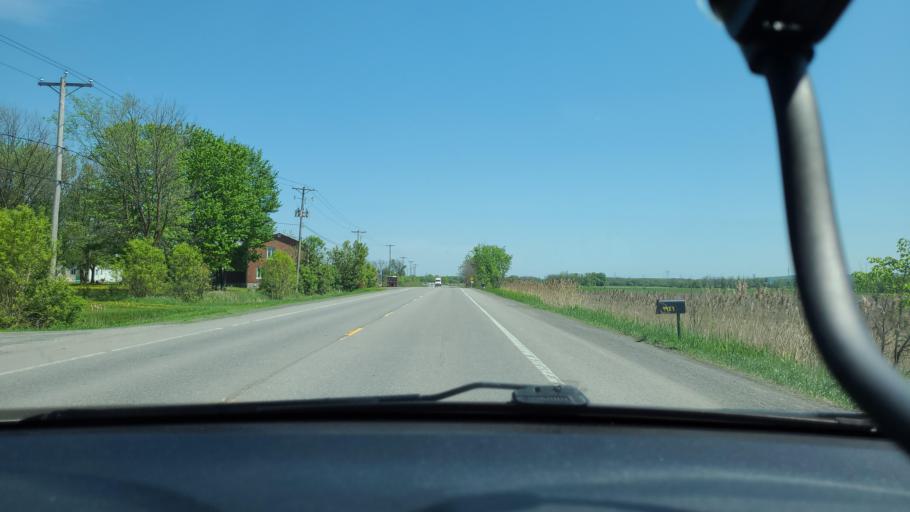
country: CA
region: Quebec
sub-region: Laurentides
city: Mirabel
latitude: 45.6124
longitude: -74.0823
